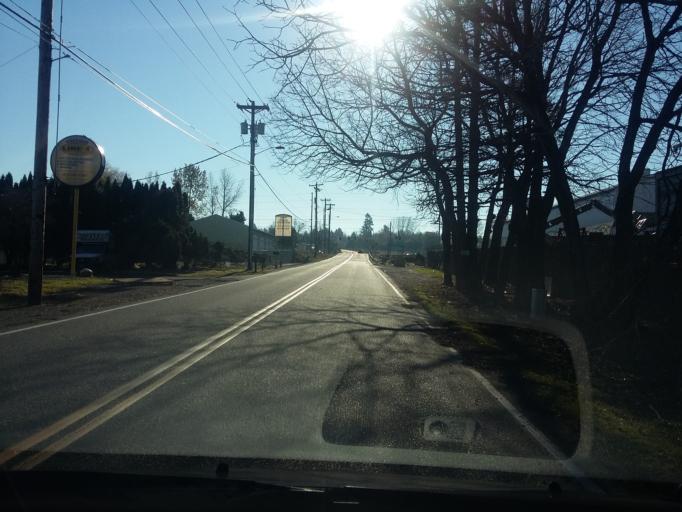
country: US
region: Oregon
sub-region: Multnomah County
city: Fairview
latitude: 45.5543
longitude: -122.5103
